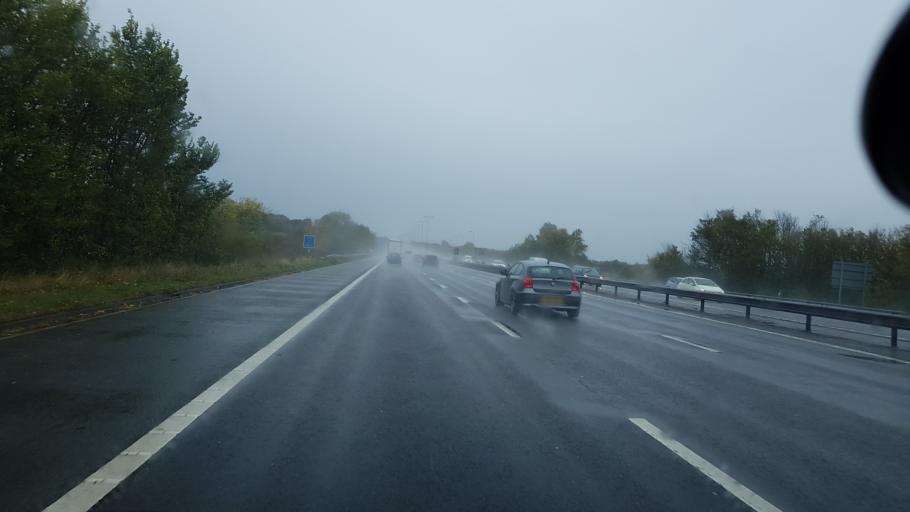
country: GB
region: England
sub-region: Worcestershire
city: Bredon
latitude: 52.0375
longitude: -2.1296
